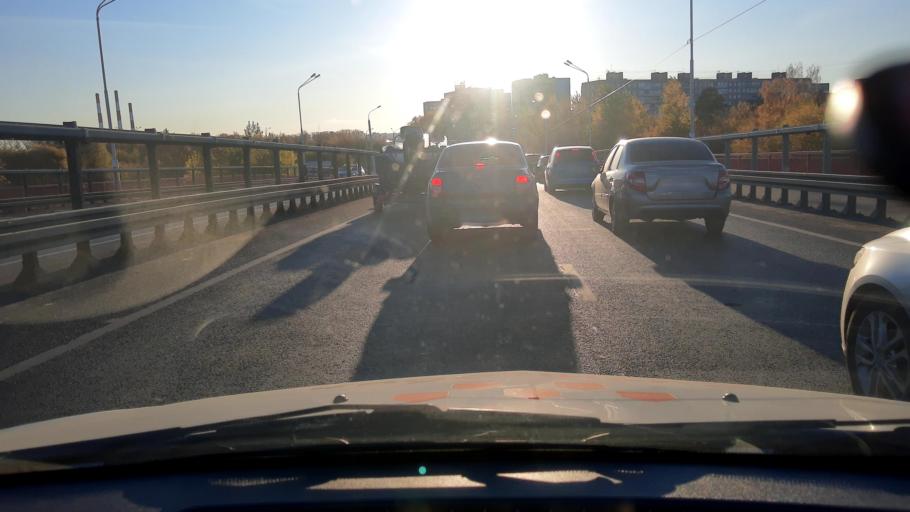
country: RU
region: Bashkortostan
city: Ufa
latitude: 54.8039
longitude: 56.1403
